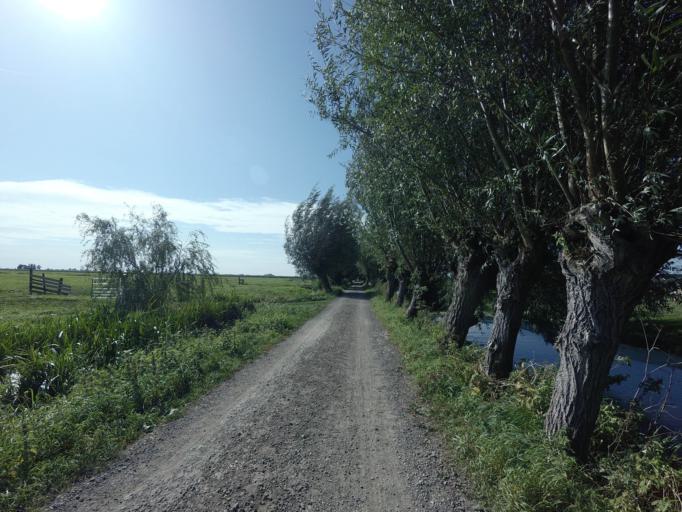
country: NL
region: South Holland
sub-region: Molenwaard
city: Liesveld
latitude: 51.9163
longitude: 4.7964
